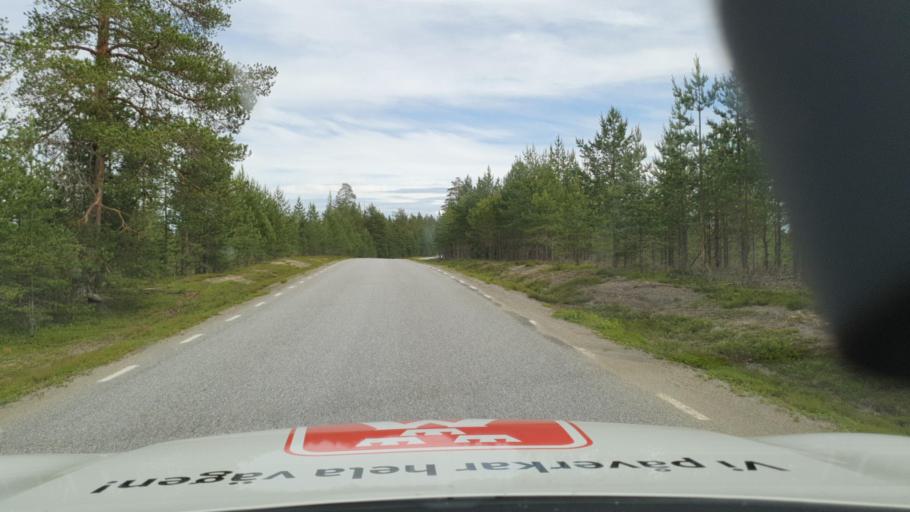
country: SE
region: Vaesterbotten
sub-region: Skelleftea Kommun
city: Burtraesk
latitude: 64.5055
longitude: 20.7967
